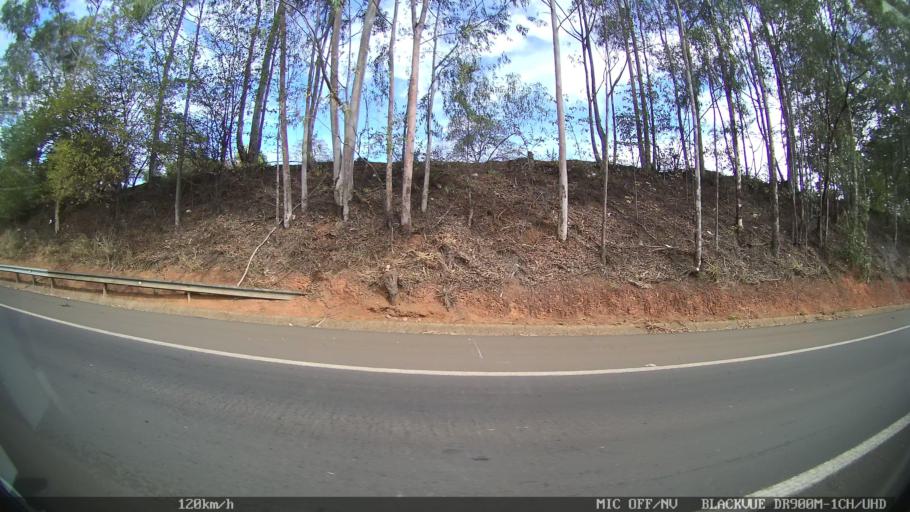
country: BR
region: Sao Paulo
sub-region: Taquaritinga
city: Taquaritinga
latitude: -21.5391
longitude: -48.5067
